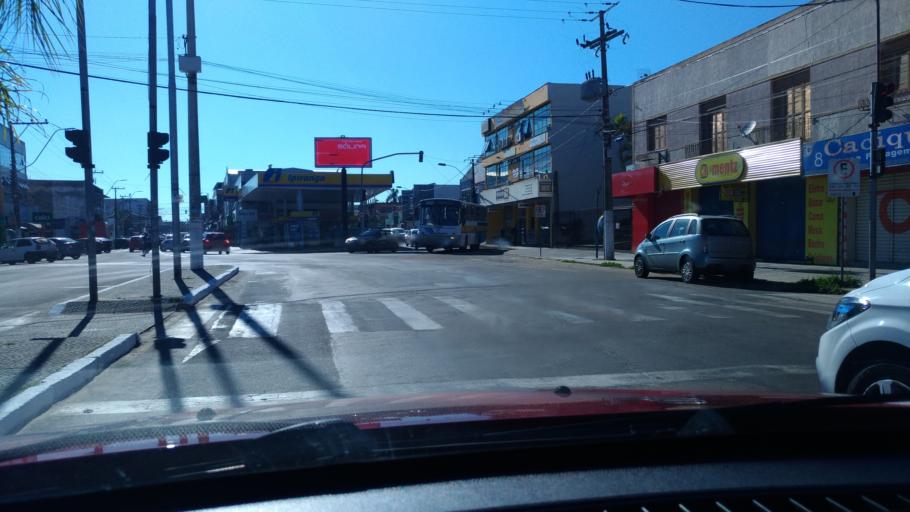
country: BR
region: Rio Grande do Sul
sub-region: Viamao
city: Viamao
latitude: -30.0828
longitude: -51.0299
